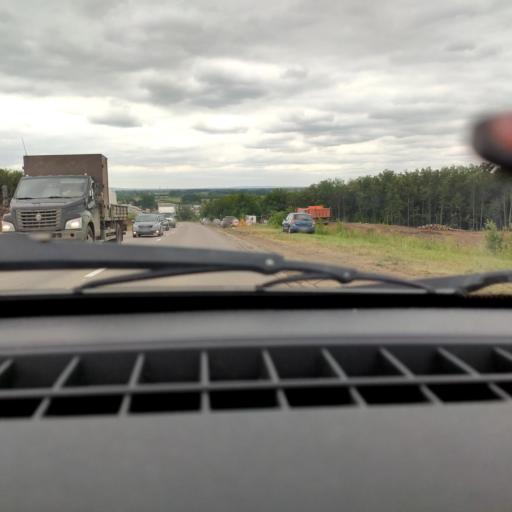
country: RU
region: Bashkortostan
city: Kabakovo
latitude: 54.6956
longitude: 56.1468
